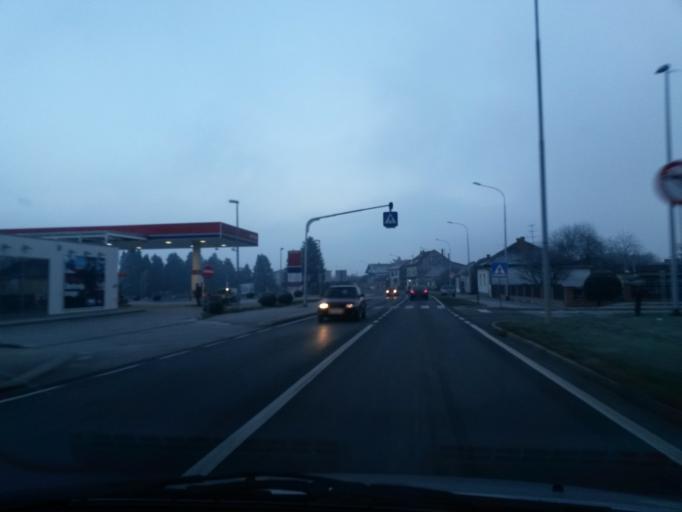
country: HR
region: Koprivnicko-Krizevacka
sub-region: Grad Koprivnica
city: Koprivnica
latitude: 46.1726
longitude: 16.8117
